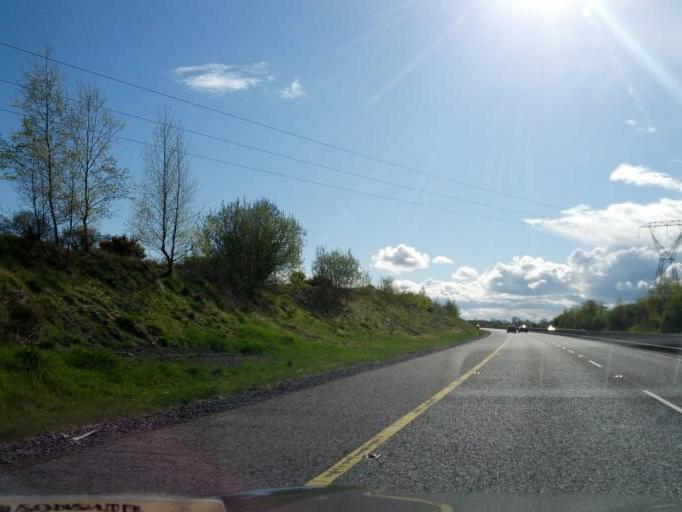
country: IE
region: Leinster
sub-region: An Iarmhi
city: Rathwire
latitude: 53.4473
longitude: -7.1917
